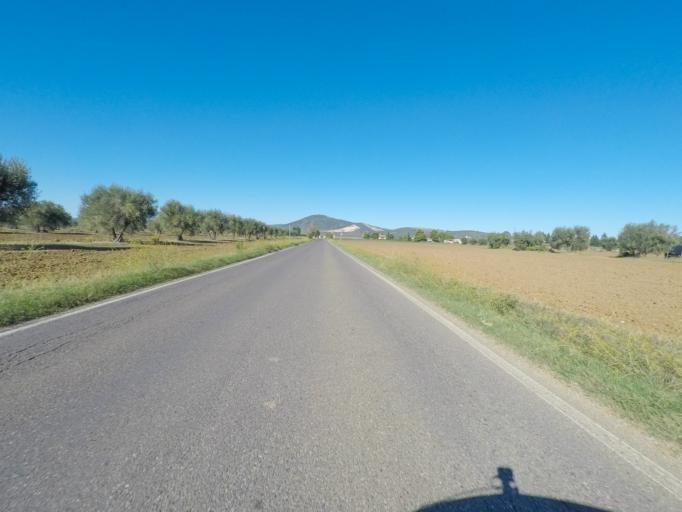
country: IT
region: Tuscany
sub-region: Provincia di Grosseto
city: Grosseto
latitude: 42.7711
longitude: 11.1392
